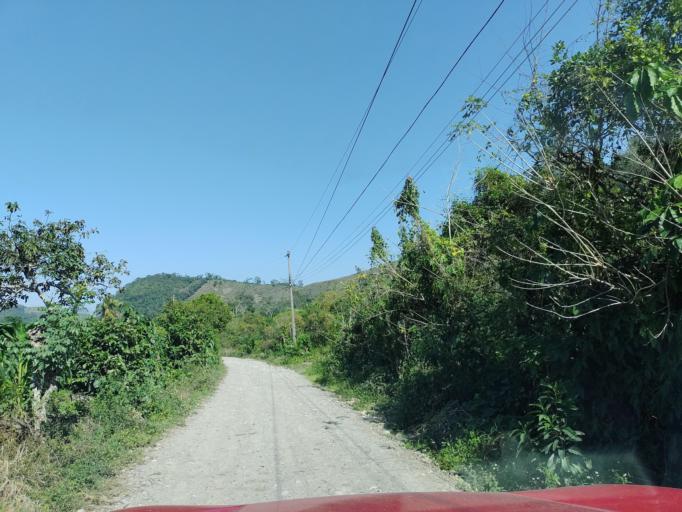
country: MX
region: Veracruz
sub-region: Papantla
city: Polutla
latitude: 20.4837
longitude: -97.1922
